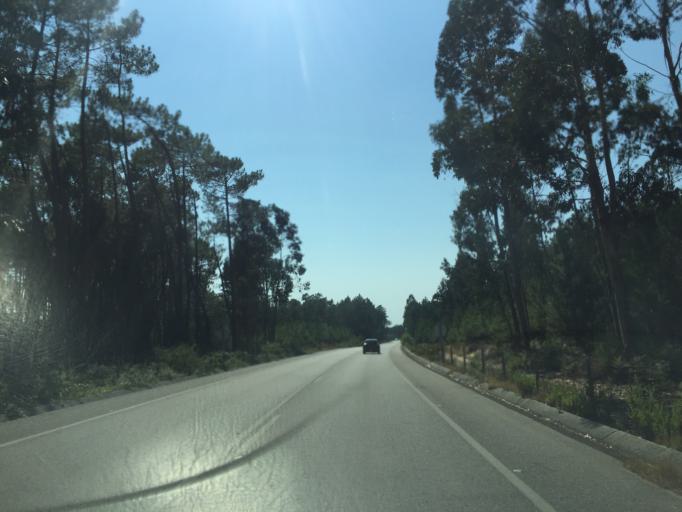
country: PT
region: Coimbra
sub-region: Montemor-O-Velho
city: Arazede
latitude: 40.3231
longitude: -8.6838
